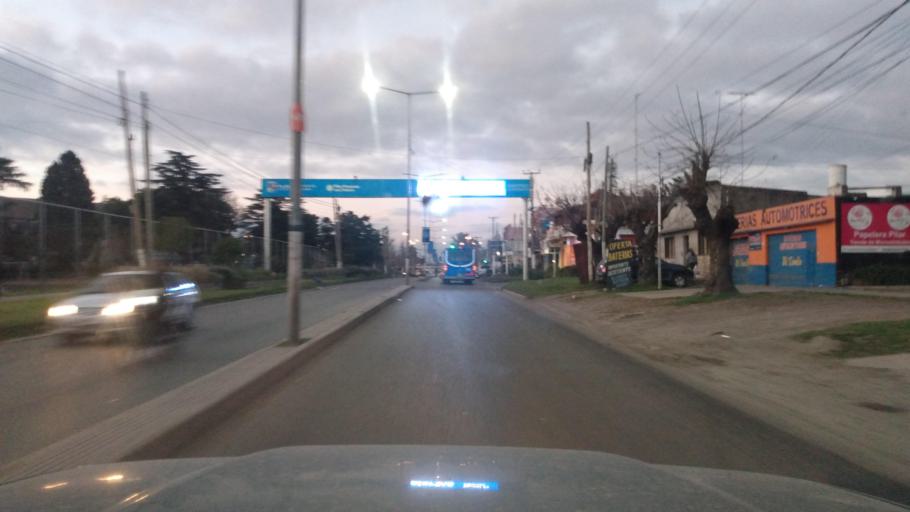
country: AR
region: Buenos Aires
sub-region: Partido de Pilar
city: Pilar
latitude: -34.4522
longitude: -58.9076
